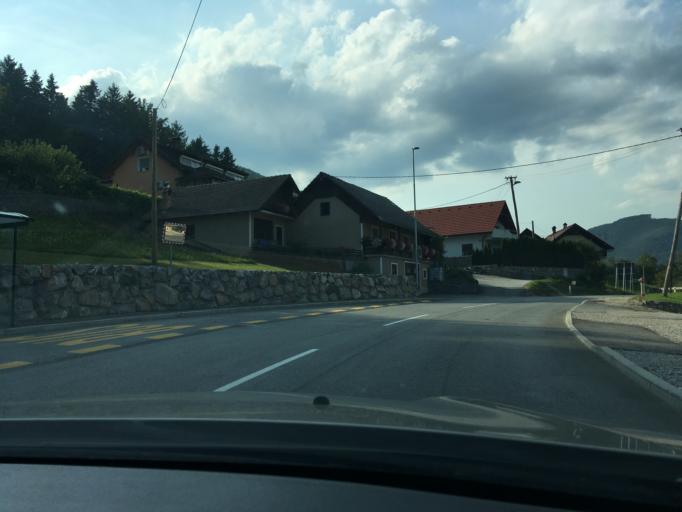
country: SI
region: Dolenjske Toplice
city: Dolenjske Toplice
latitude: 45.7596
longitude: 15.0314
